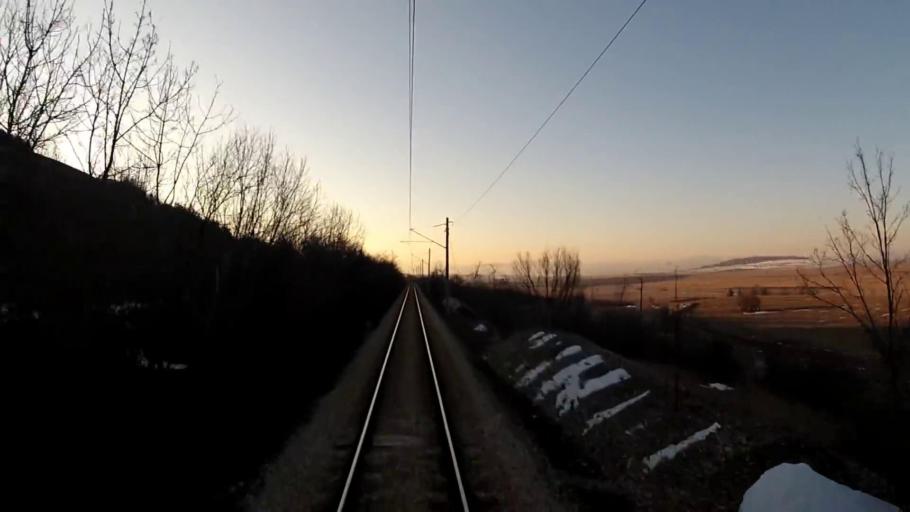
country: BG
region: Sofiya
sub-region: Obshtina Dragoman
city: Dragoman
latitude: 42.9014
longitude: 22.9498
